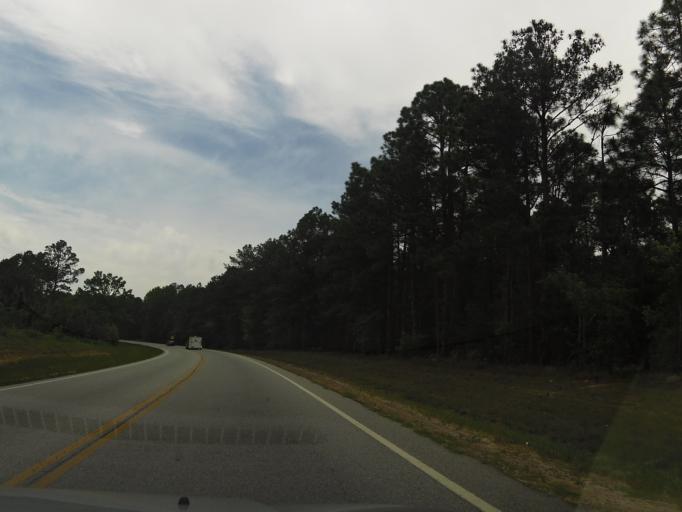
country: US
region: Georgia
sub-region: Emanuel County
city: Swainsboro
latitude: 32.5114
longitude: -82.2633
